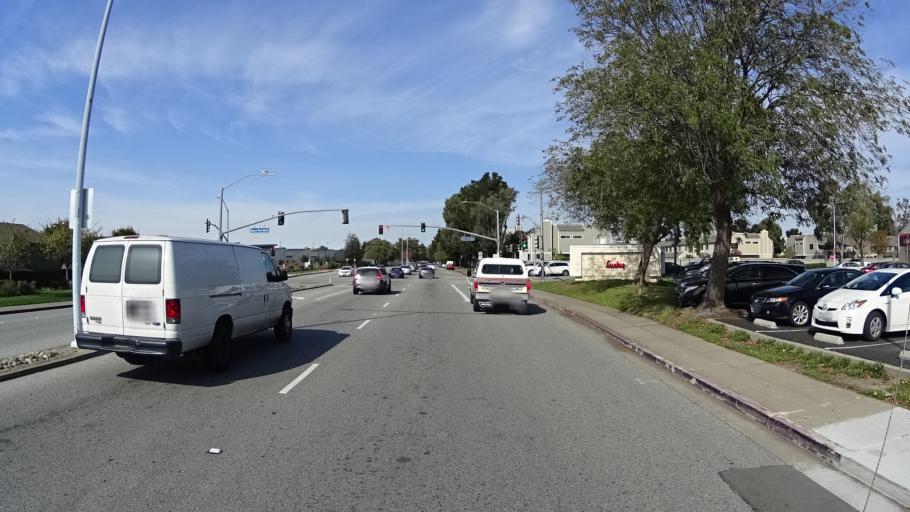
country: US
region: California
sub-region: San Mateo County
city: Foster City
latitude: 37.5453
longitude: -122.2719
